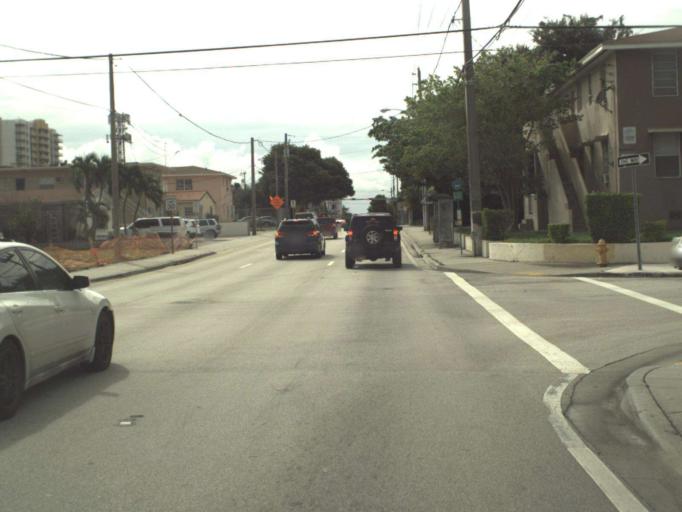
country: US
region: Florida
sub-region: Miami-Dade County
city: Miami
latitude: 25.7671
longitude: -80.2056
